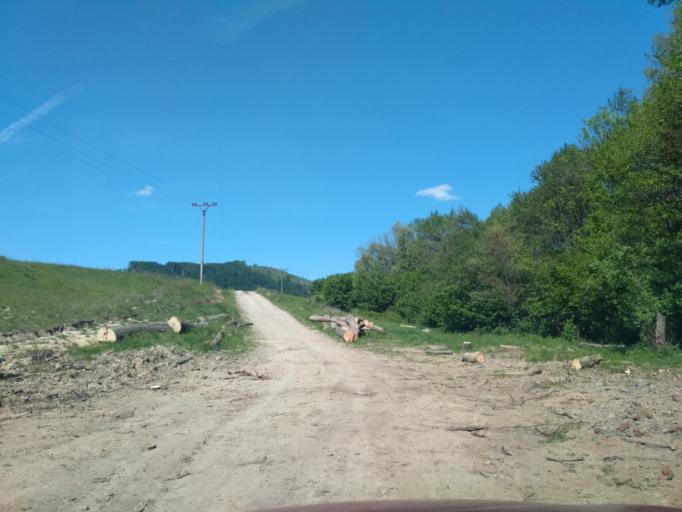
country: SK
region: Presovsky
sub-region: Okres Presov
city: Presov
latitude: 48.8908
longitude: 21.3918
